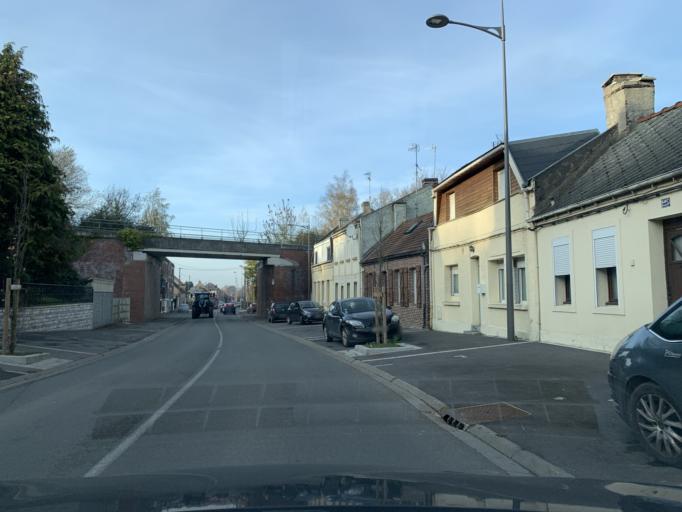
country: FR
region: Nord-Pas-de-Calais
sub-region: Departement du Nord
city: Cambrai
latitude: 50.1606
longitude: 3.2507
